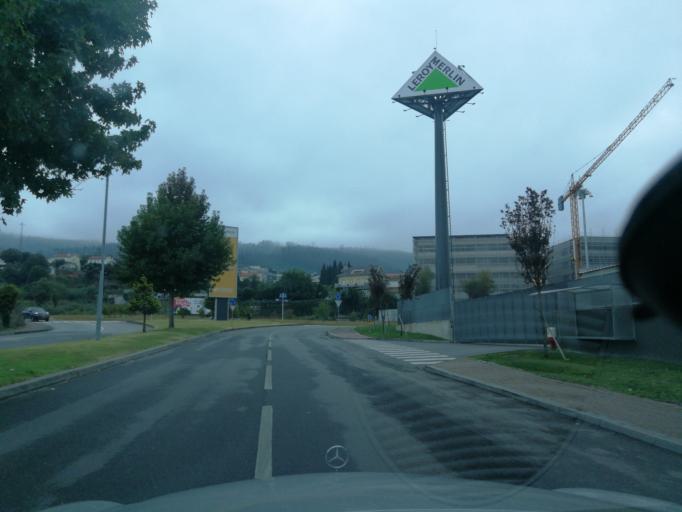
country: PT
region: Braga
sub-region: Braga
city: Braga
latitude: 41.5474
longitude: -8.3982
